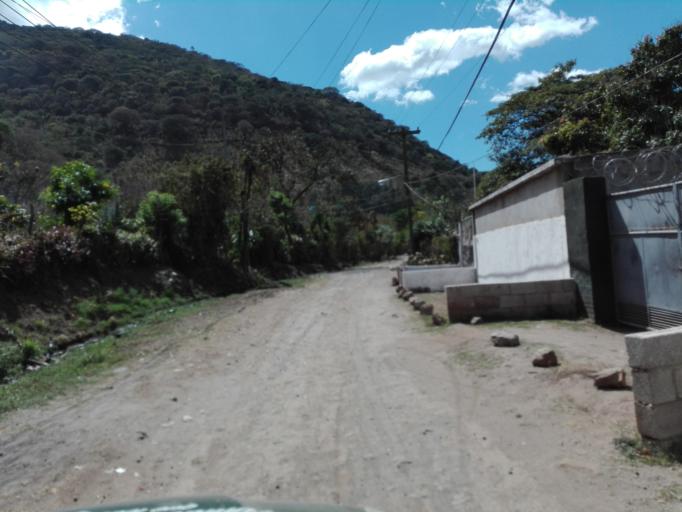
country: GT
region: Guatemala
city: Amatitlan
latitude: 14.4719
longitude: -90.6035
